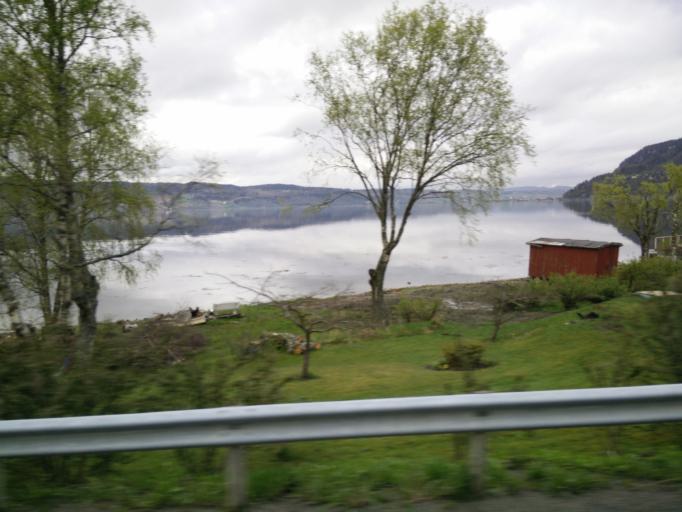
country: NO
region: Sor-Trondelag
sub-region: Skaun
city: Borsa
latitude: 63.3152
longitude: 10.1527
